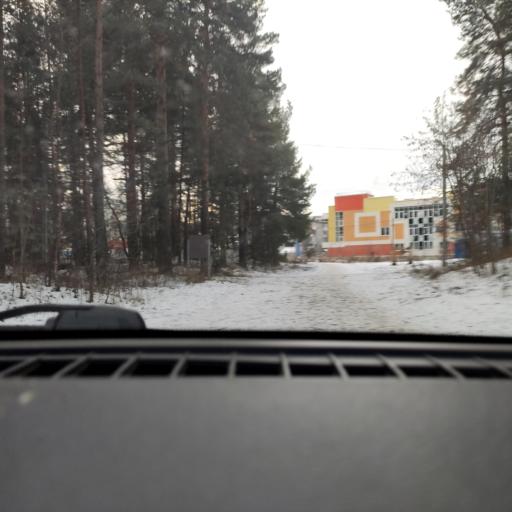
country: RU
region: Perm
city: Kondratovo
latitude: 58.0392
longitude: 56.1363
